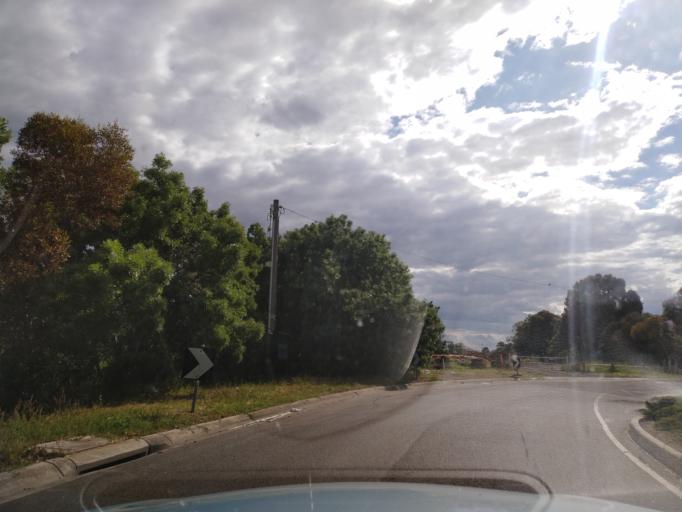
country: AU
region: Victoria
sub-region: Hobsons Bay
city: South Kingsville
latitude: -37.8483
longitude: 144.8635
